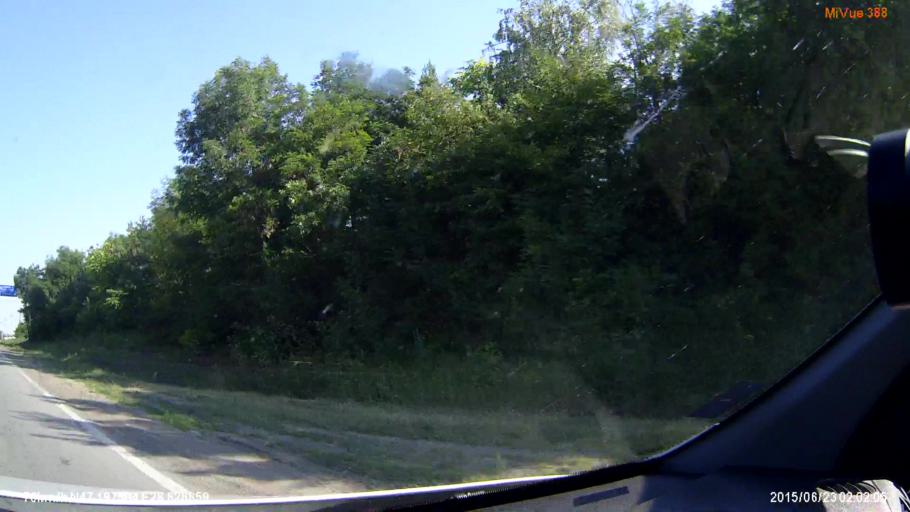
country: MD
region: Straseni
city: Straseni
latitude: 47.1977
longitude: 28.6263
